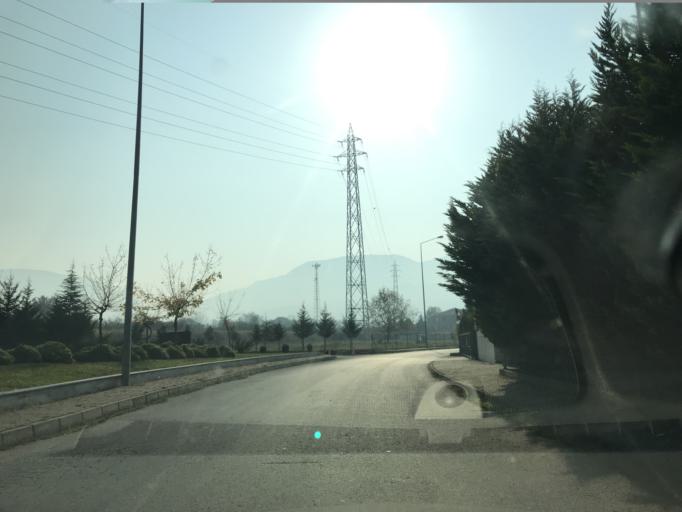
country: TR
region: Duzce
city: Duzce
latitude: 40.7848
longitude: 31.1536
